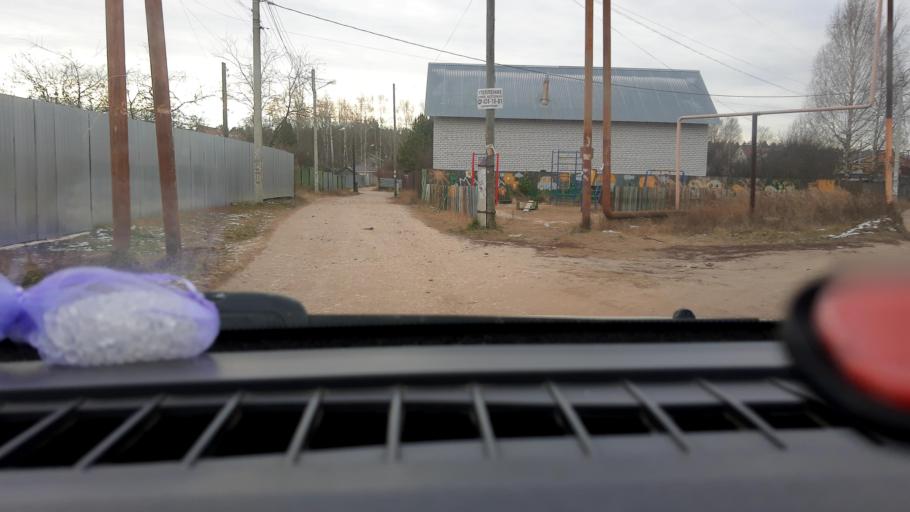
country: RU
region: Nizjnij Novgorod
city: Gorbatovka
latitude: 56.3840
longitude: 43.7749
